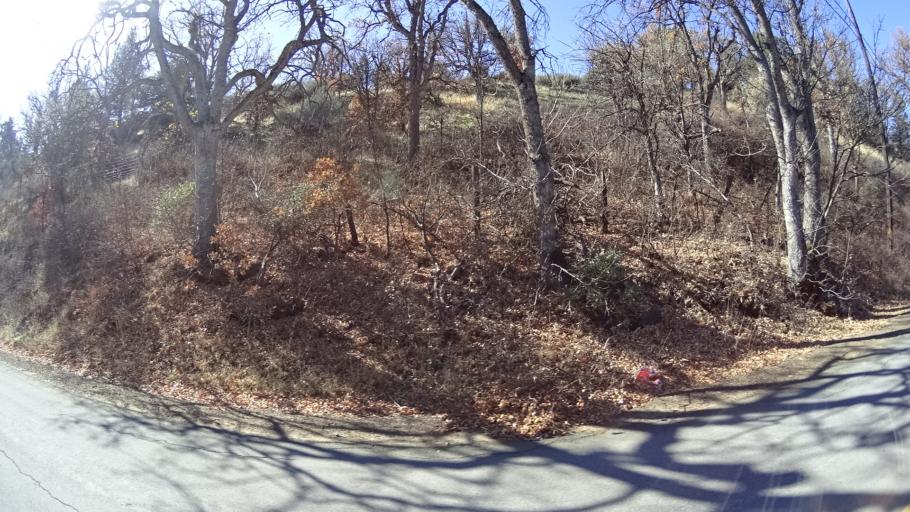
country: US
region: California
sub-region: Siskiyou County
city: Montague
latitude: 41.9166
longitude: -122.5642
